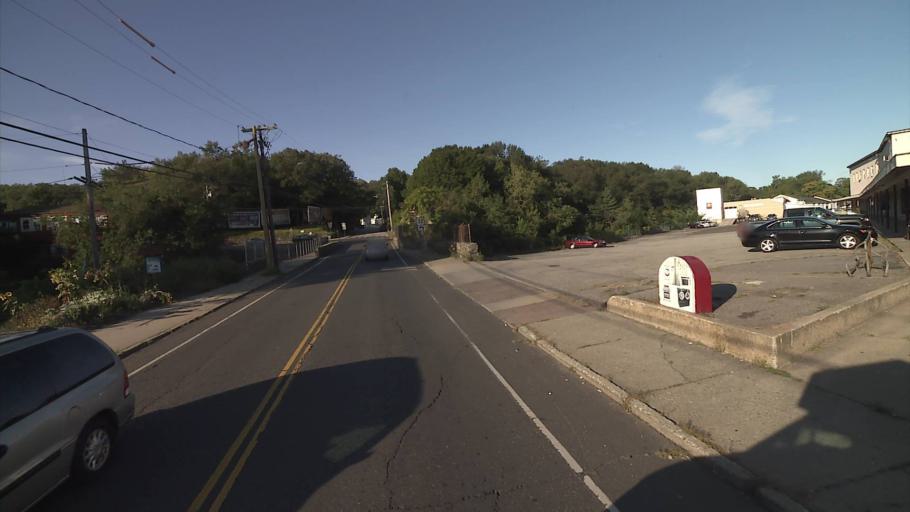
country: US
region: Connecticut
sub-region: Windham County
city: Willimantic
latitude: 41.7121
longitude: -72.2195
